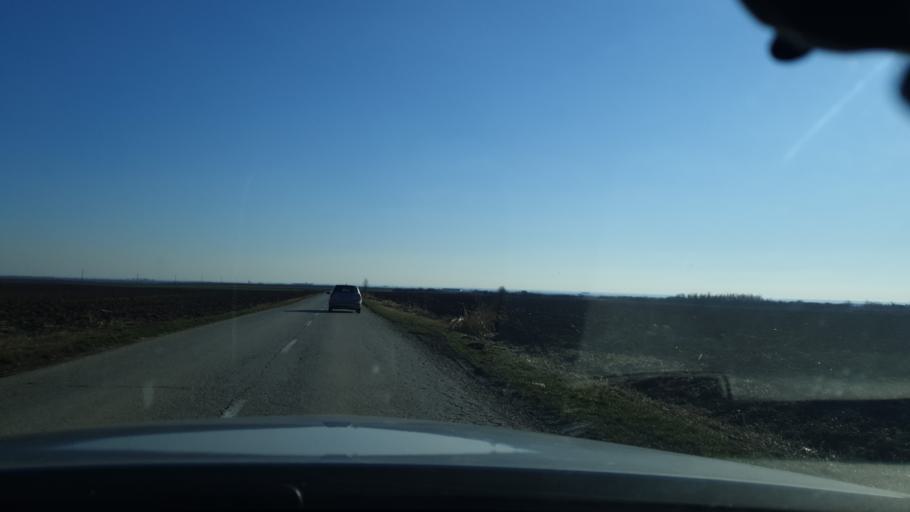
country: RS
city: Vrdnik
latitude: 45.0755
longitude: 19.8086
